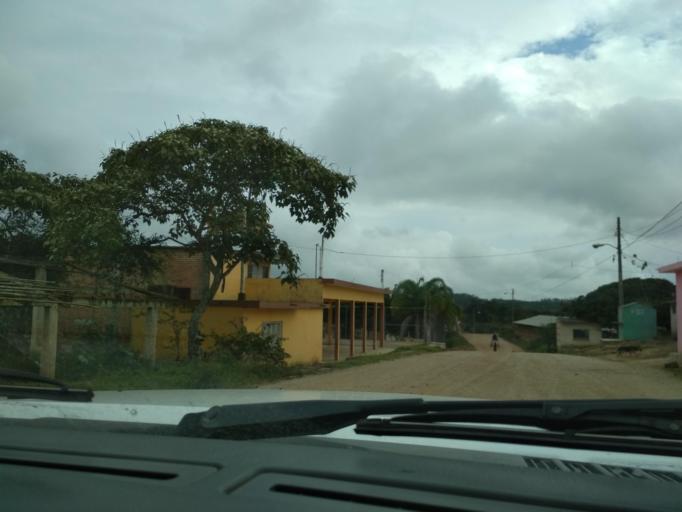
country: MX
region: Veracruz
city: El Castillo
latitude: 19.5445
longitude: -96.8487
